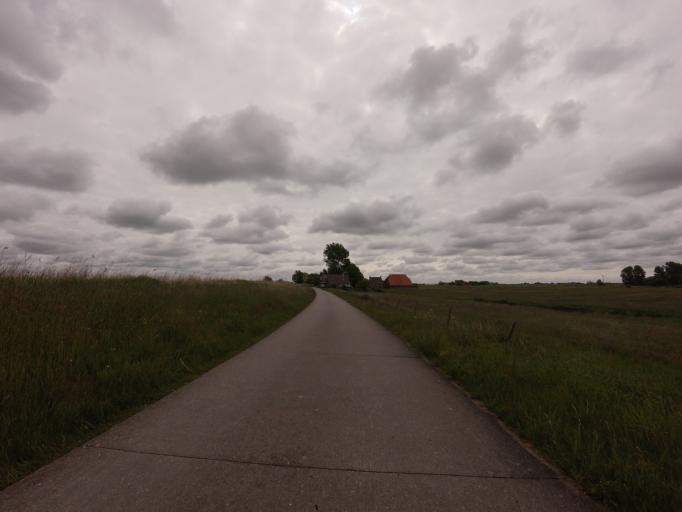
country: NL
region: Friesland
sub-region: Sudwest Fryslan
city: Workum
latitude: 53.0024
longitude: 5.4630
